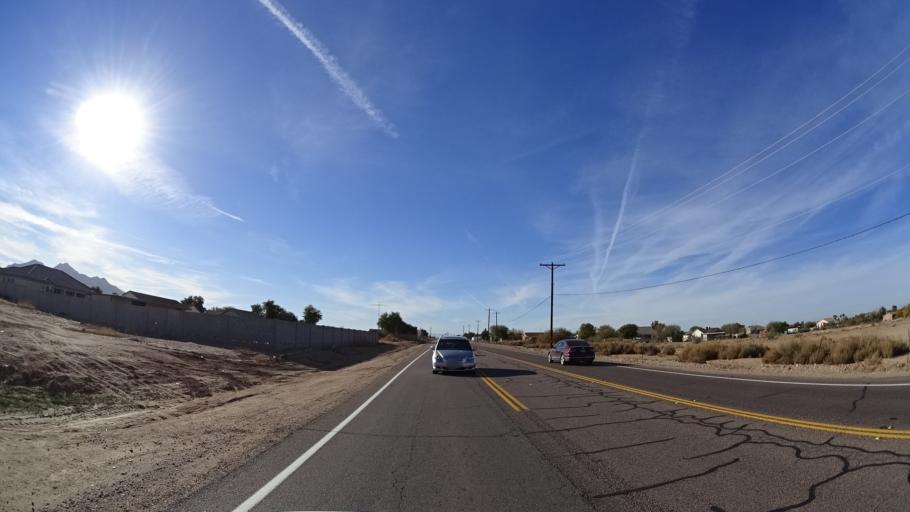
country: US
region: Arizona
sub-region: Maricopa County
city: Queen Creek
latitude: 33.2194
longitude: -111.6700
